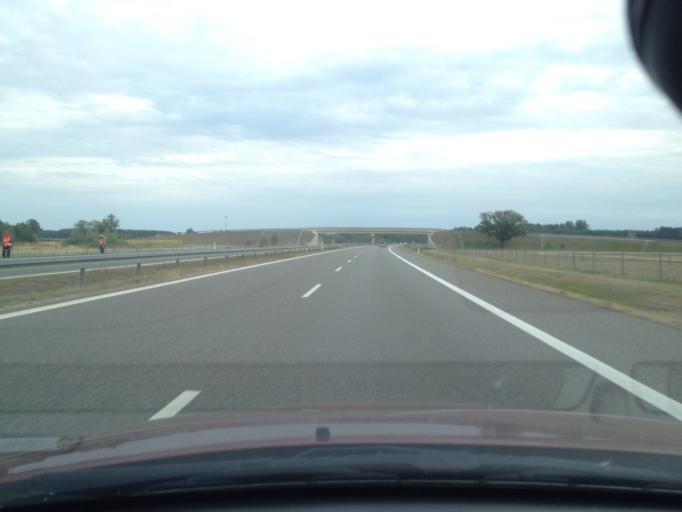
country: PL
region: West Pomeranian Voivodeship
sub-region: Powiat pyrzycki
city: Lipiany
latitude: 52.9442
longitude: 14.9687
